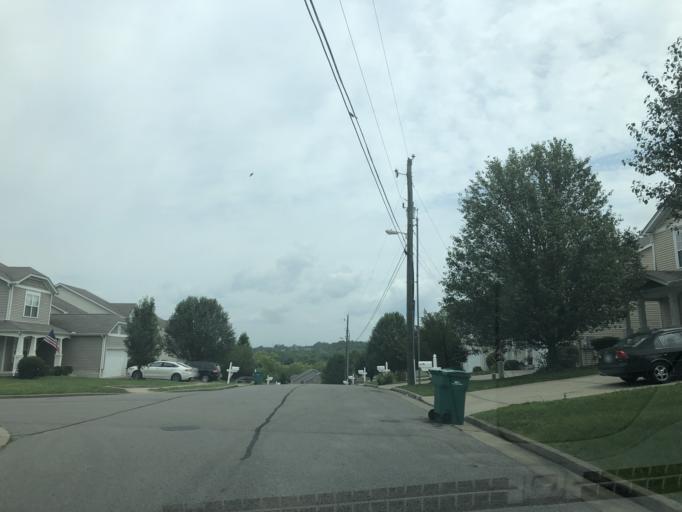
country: US
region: Tennessee
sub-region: Williamson County
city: Nolensville
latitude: 36.0208
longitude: -86.6719
